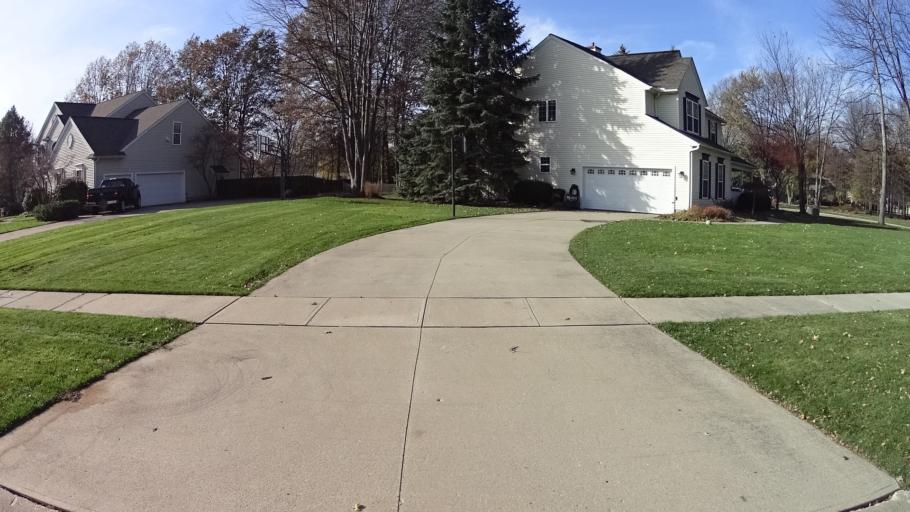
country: US
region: Ohio
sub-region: Lorain County
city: Avon Lake
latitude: 41.5042
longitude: -81.9955
